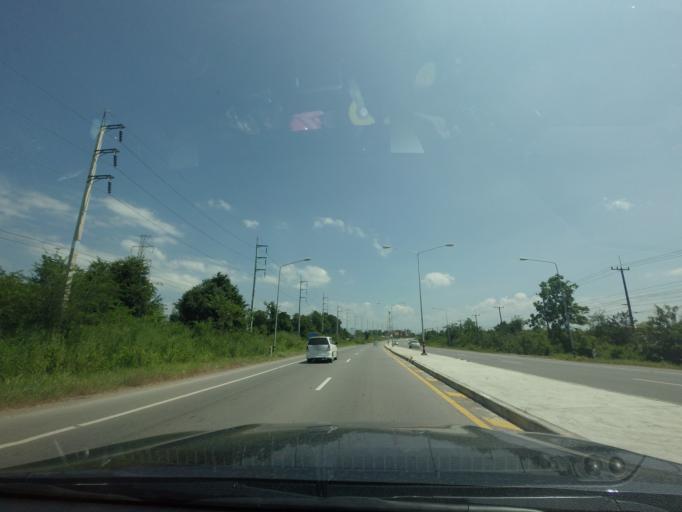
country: TH
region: Phetchabun
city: Lom Sak
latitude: 16.7691
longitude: 101.1760
